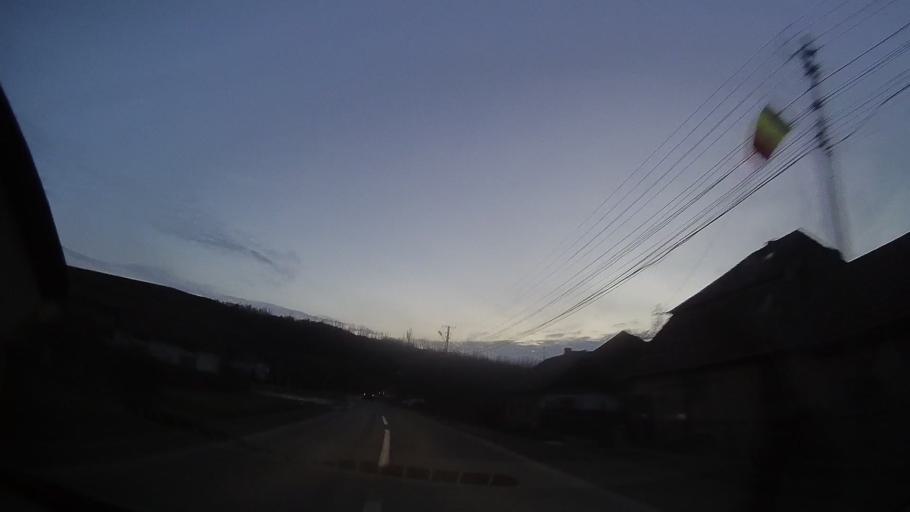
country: RO
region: Mures
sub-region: Comuna Sarmasu
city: Sarmasu
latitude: 46.7656
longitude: 24.1877
